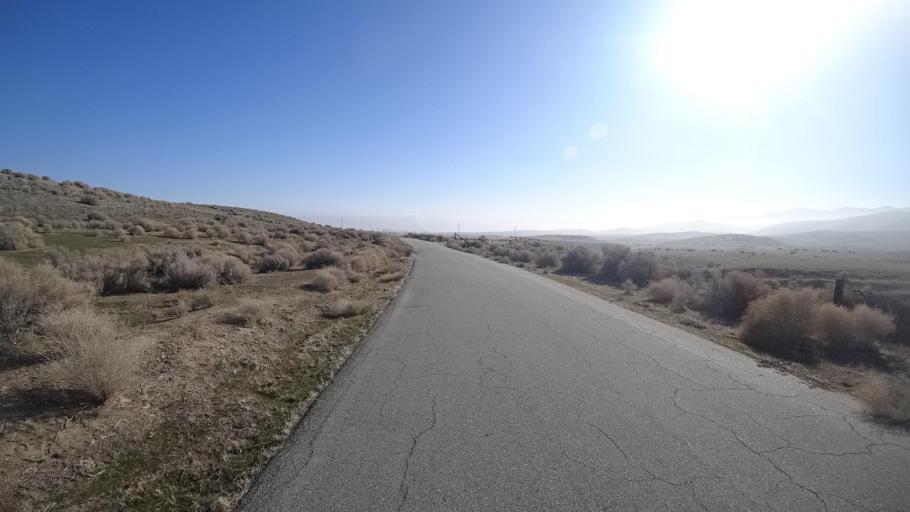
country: US
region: California
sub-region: Kern County
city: Taft Heights
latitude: 35.2286
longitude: -119.6421
